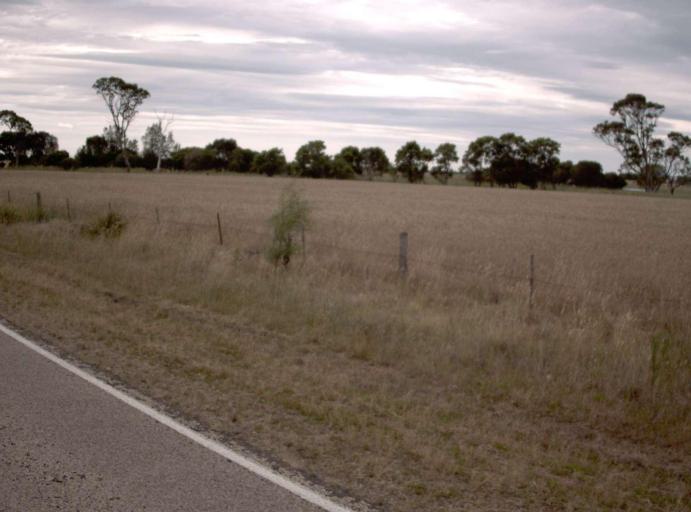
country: AU
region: Victoria
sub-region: East Gippsland
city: Bairnsdale
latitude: -37.9587
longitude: 147.4992
